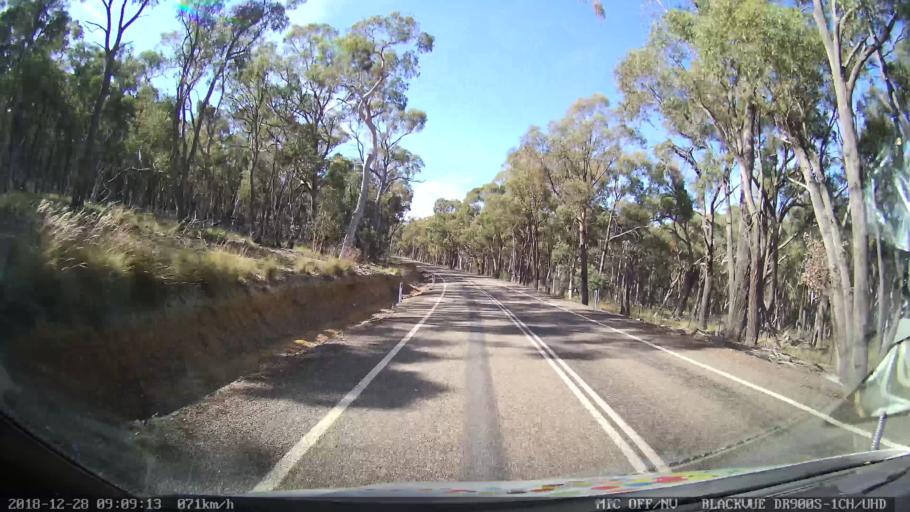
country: AU
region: New South Wales
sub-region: Upper Lachlan Shire
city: Crookwell
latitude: -34.2192
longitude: 149.3354
